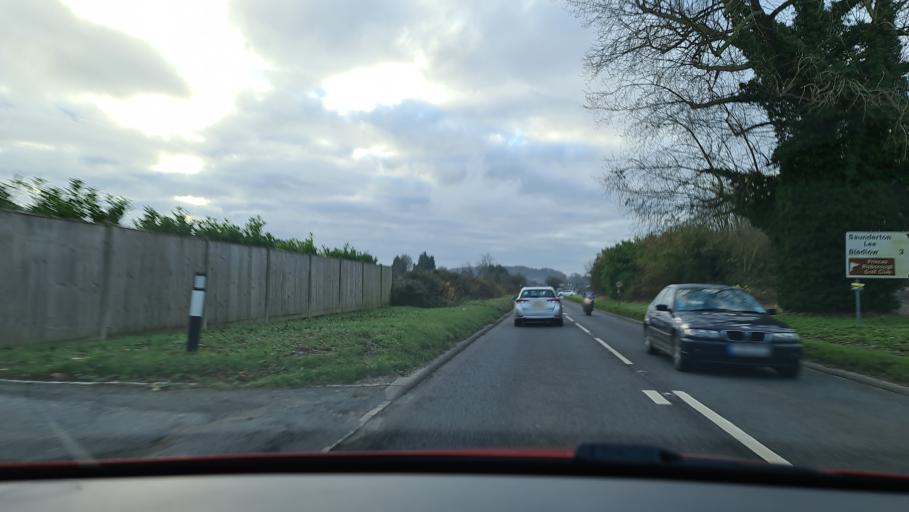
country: GB
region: England
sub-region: Buckinghamshire
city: Princes Risborough
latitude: 51.6913
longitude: -0.8328
